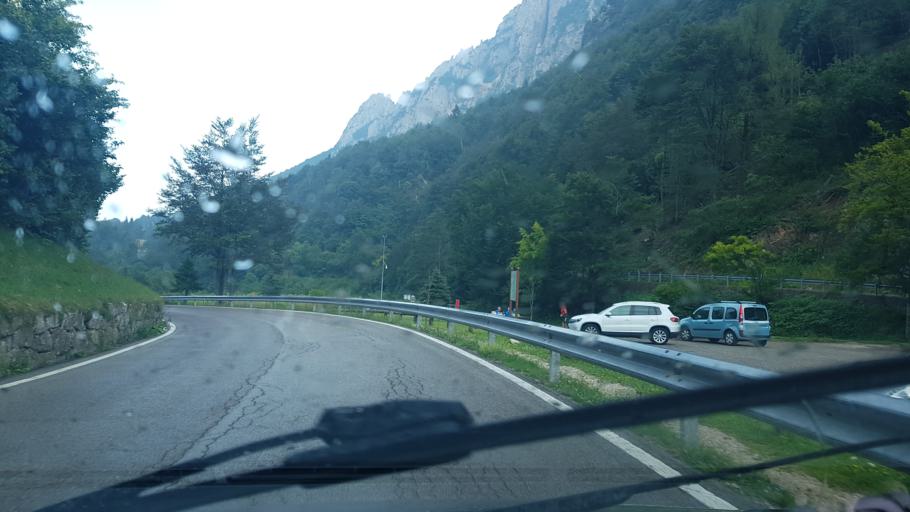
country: IT
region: Trentino-Alto Adige
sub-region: Provincia di Trento
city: Vallarsa
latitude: 45.7596
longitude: 11.1741
